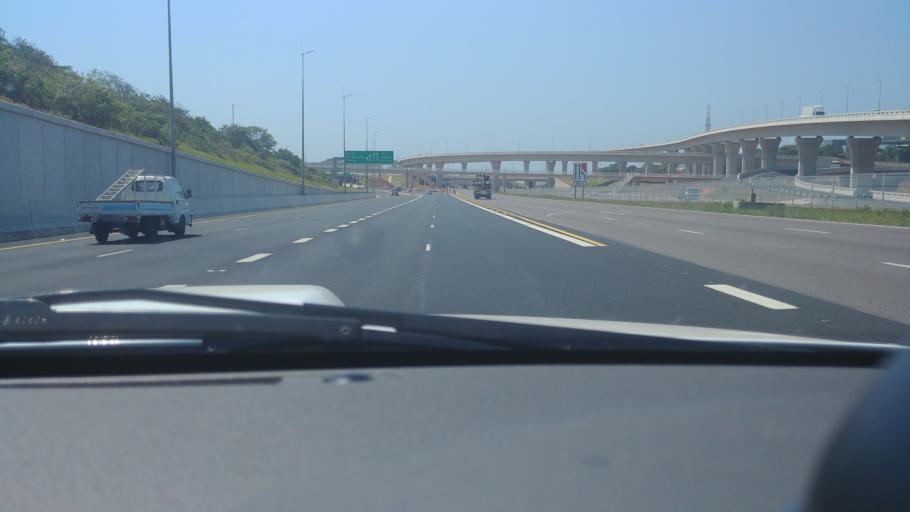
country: ZA
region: KwaZulu-Natal
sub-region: eThekwini Metropolitan Municipality
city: Durban
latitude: -29.7278
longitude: 31.0569
